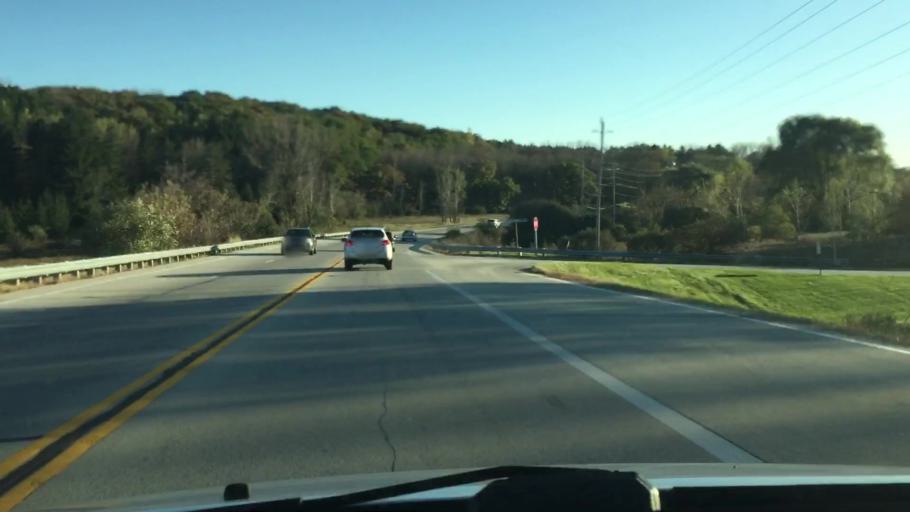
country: US
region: Wisconsin
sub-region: Waukesha County
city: Wales
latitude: 43.0343
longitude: -88.3742
